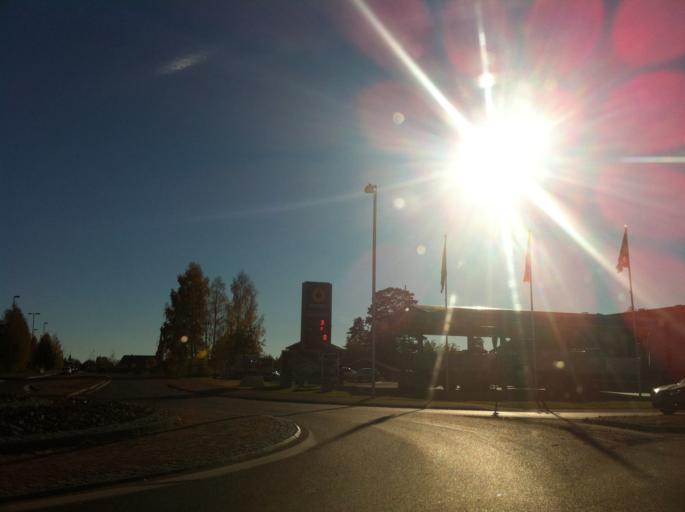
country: SE
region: Dalarna
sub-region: Mora Kommun
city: Mora
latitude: 61.0157
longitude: 14.5389
